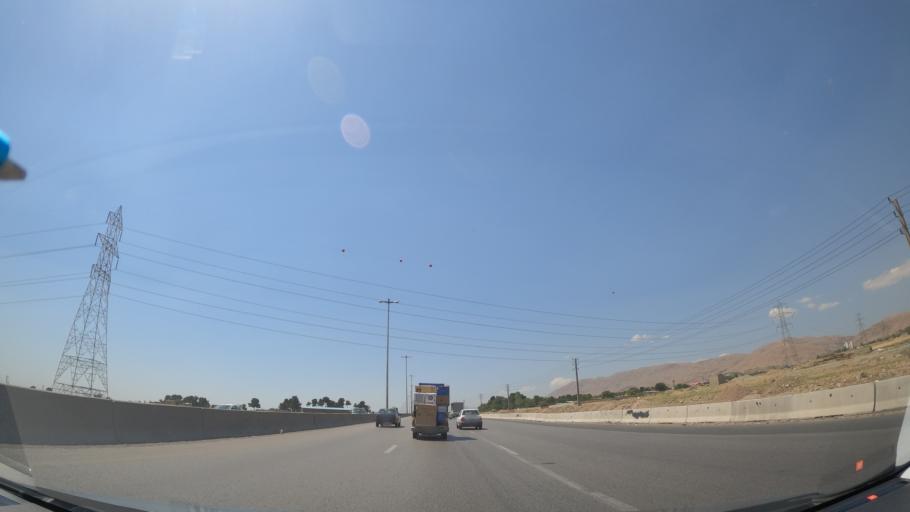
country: IR
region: Alborz
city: Karaj
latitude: 35.8707
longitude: 50.8977
